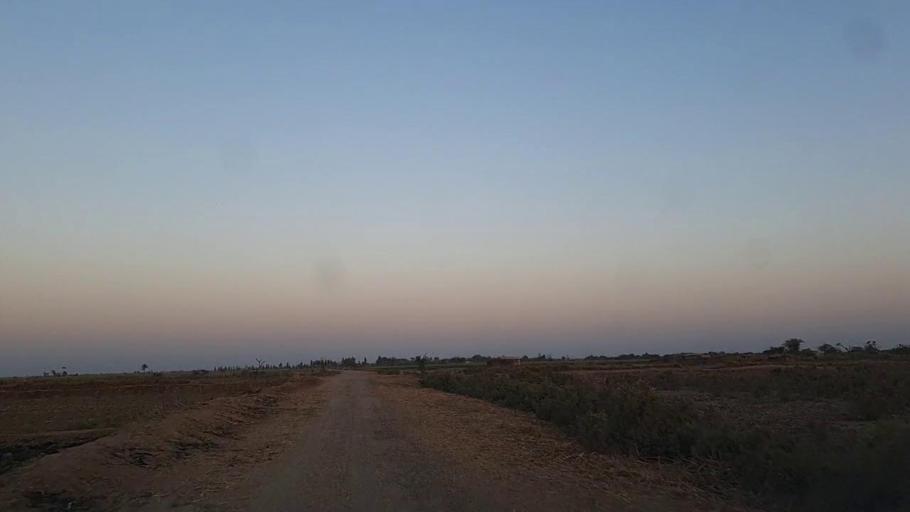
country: PK
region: Sindh
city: Samaro
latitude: 25.3106
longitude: 69.4043
